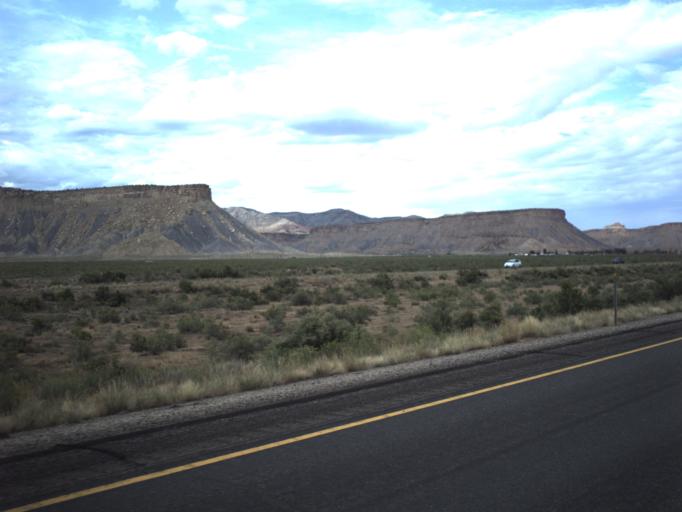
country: US
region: Utah
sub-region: Grand County
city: Moab
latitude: 38.9580
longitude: -109.7386
